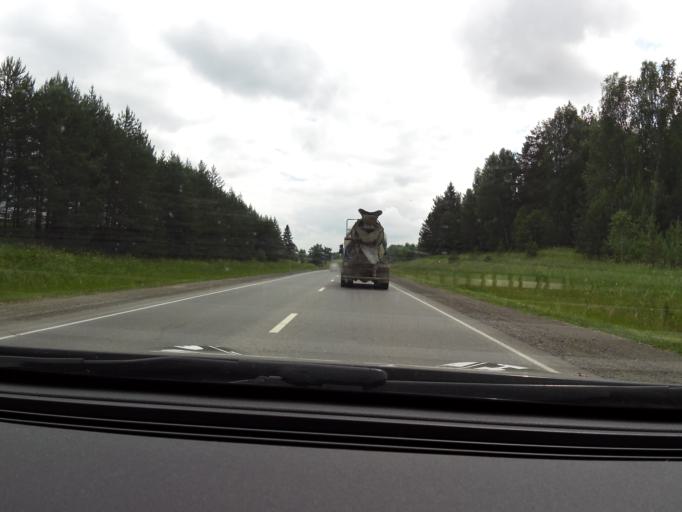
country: RU
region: Perm
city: Orda
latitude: 57.3060
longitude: 56.9796
